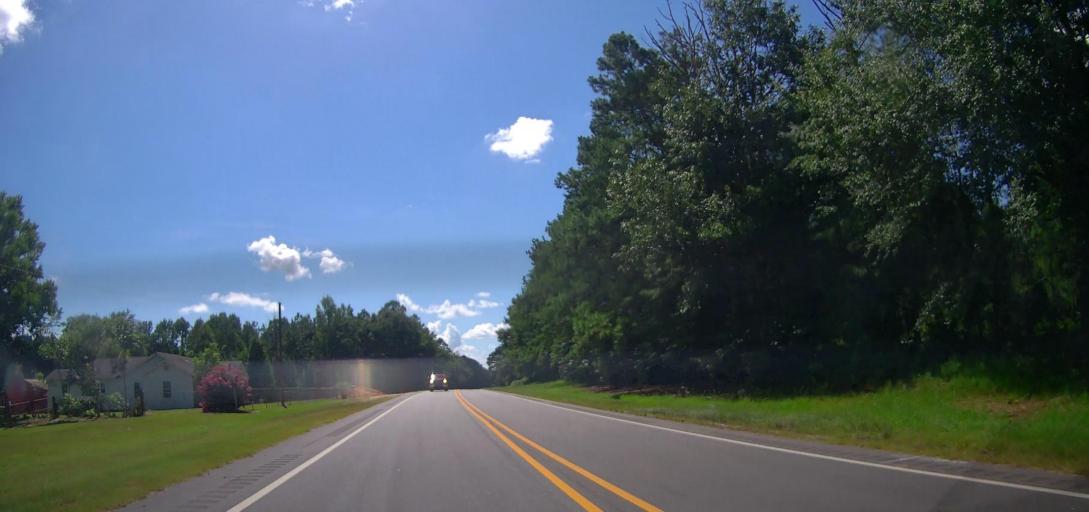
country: US
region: Alabama
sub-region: Macon County
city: Tuskegee
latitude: 32.3781
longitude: -85.7853
